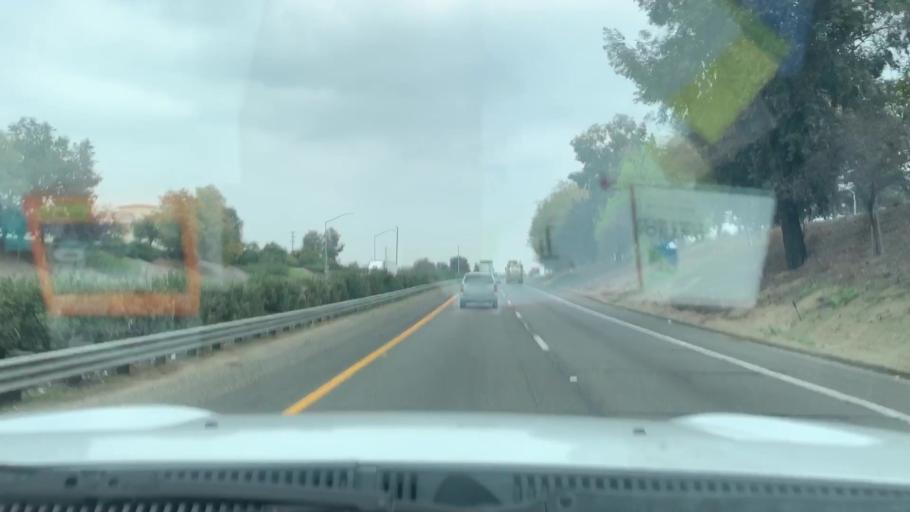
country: US
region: California
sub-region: Tulare County
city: Tulare
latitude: 36.2240
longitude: -119.3338
